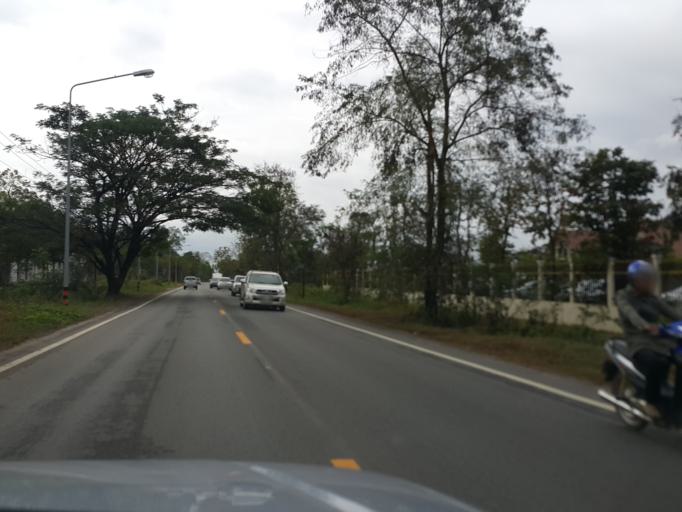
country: TH
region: Lamphun
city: Ban Thi
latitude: 18.6091
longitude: 99.0898
